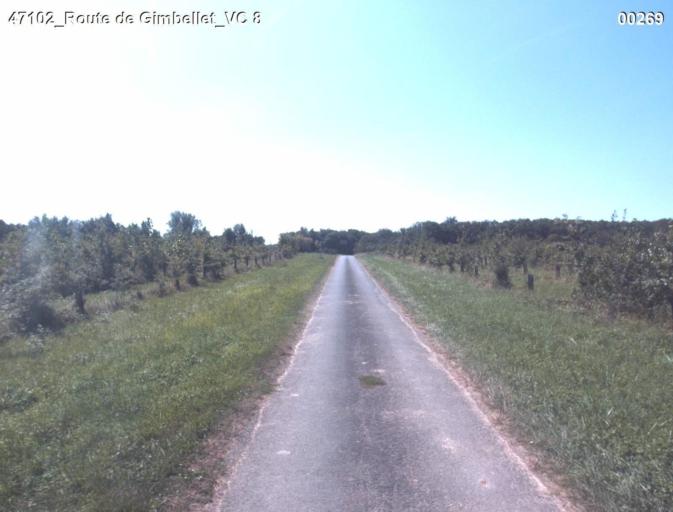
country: FR
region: Aquitaine
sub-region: Departement du Lot-et-Garonne
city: Laplume
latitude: 44.0493
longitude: 0.4466
